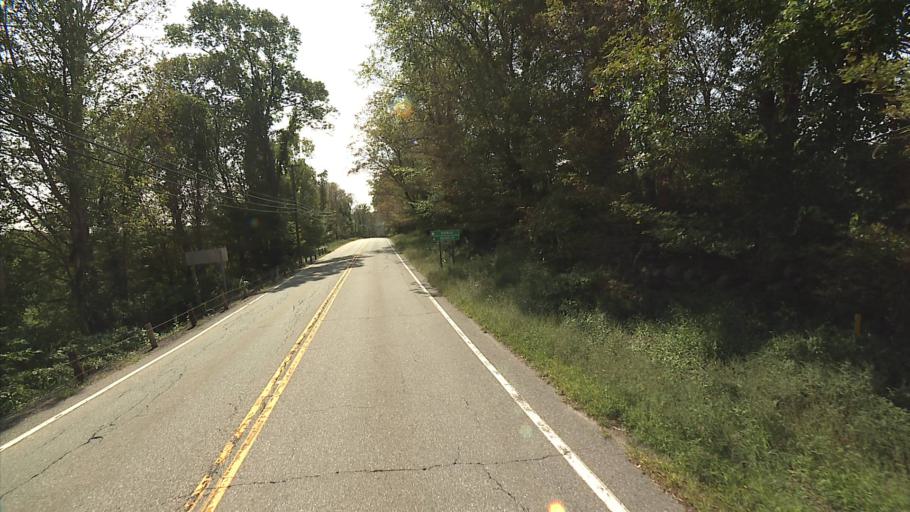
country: US
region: Connecticut
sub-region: Windham County
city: Putnam
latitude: 41.8657
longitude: -71.9600
